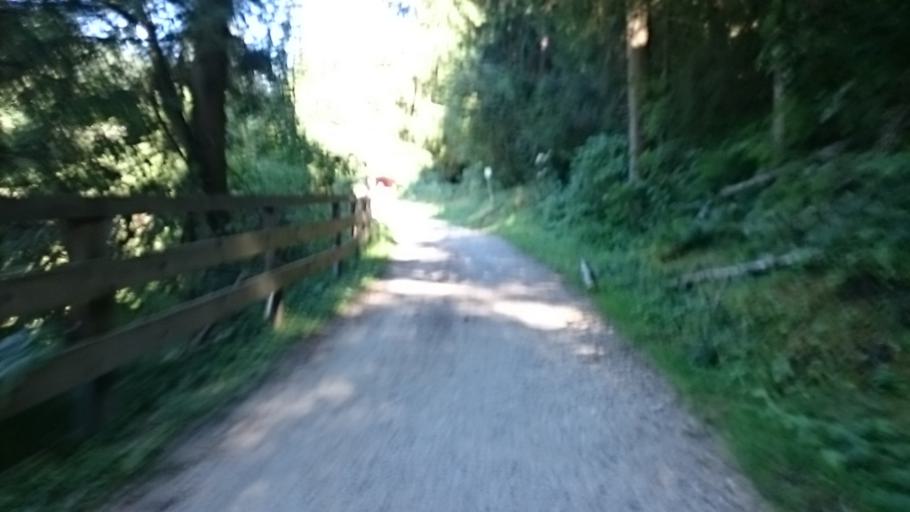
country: IT
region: Trentino-Alto Adige
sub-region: Bolzano
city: Rasun Anterselva - Rasen-Antholz
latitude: 46.7606
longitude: 12.0709
